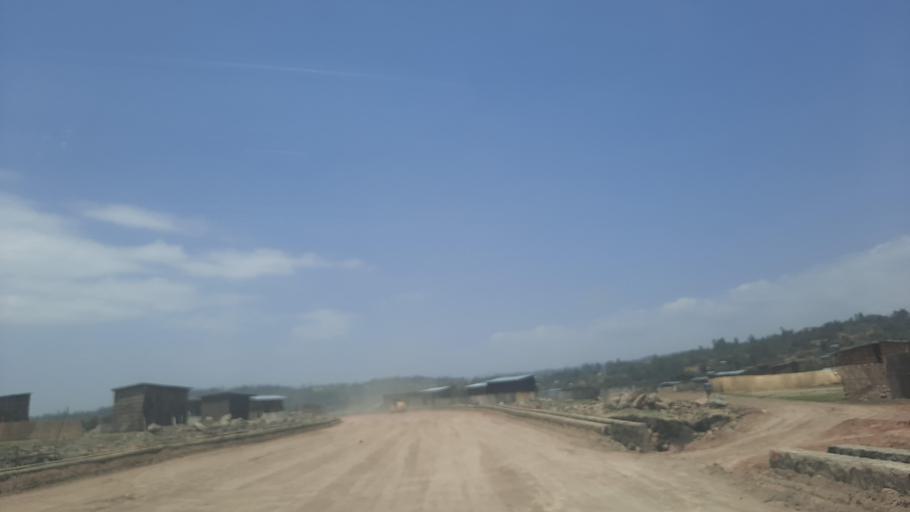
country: ET
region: Southern Nations, Nationalities, and People's Region
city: Butajira
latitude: 7.8450
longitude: 38.1737
